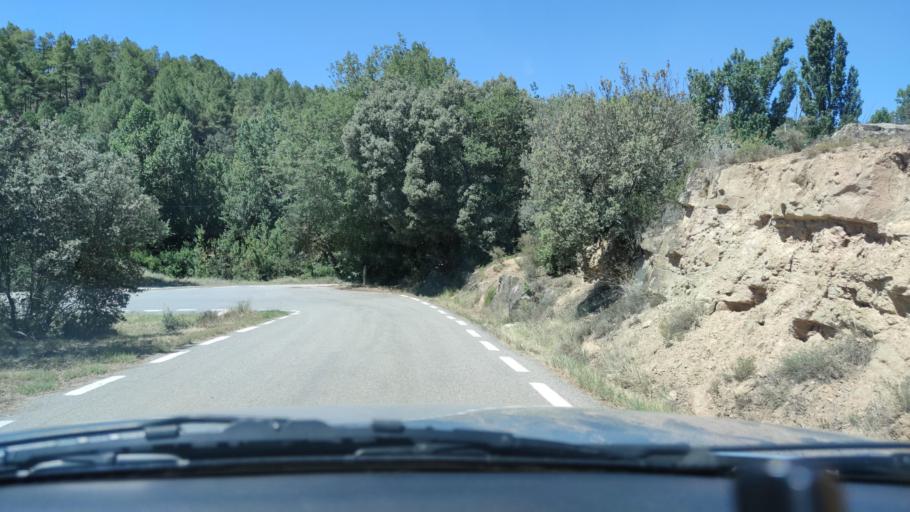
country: ES
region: Catalonia
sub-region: Provincia de Lleida
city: Tora de Riubregos
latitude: 41.8320
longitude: 1.4223
